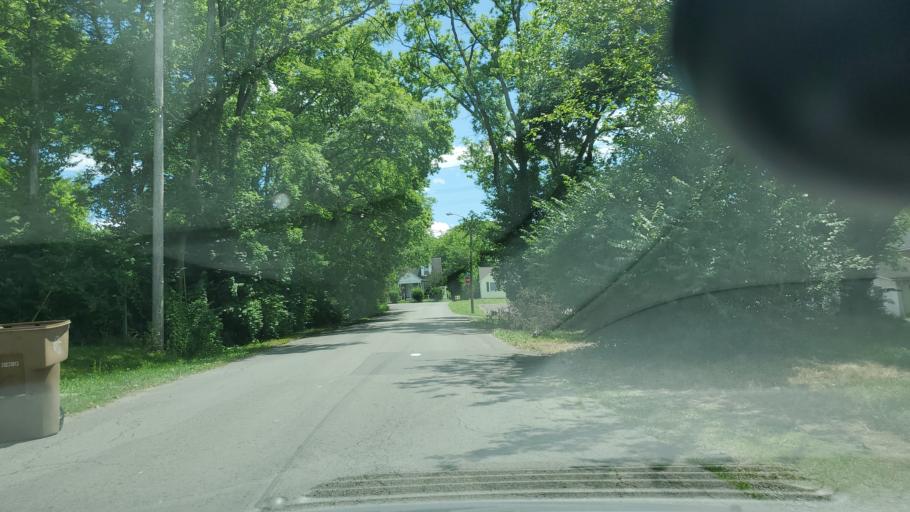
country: US
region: Tennessee
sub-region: Davidson County
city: Nashville
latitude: 36.2061
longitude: -86.7597
